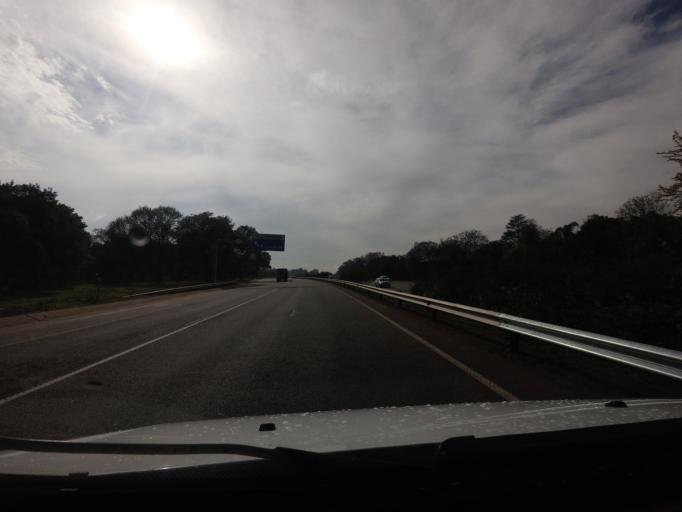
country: ZA
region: Gauteng
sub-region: City of Tshwane Metropolitan Municipality
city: Pretoria
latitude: -25.7521
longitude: 28.2998
